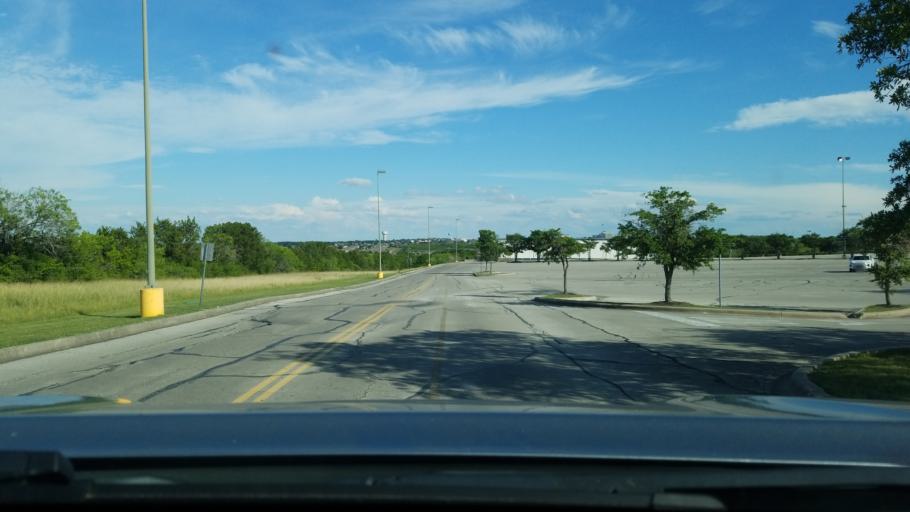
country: US
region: Texas
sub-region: Bexar County
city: Live Oak
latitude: 29.5976
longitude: -98.3478
